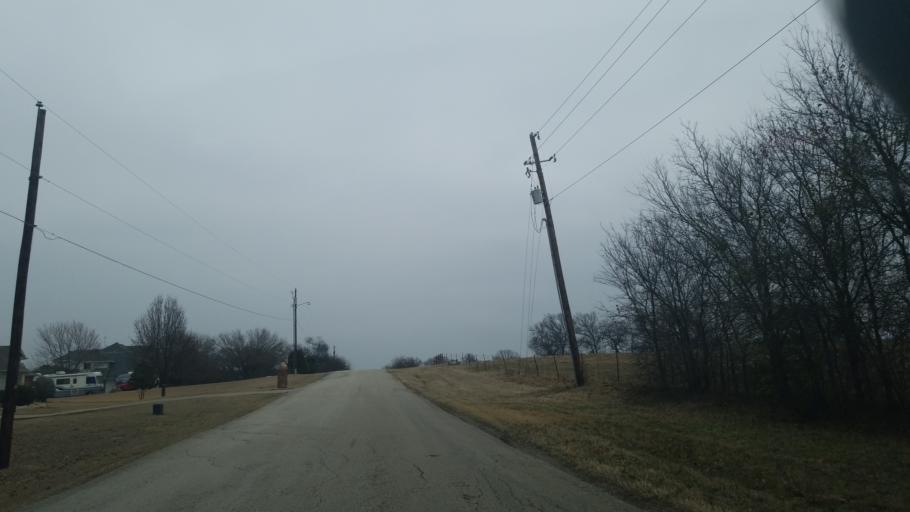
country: US
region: Texas
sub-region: Denton County
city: Argyle
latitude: 33.1472
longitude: -97.1549
